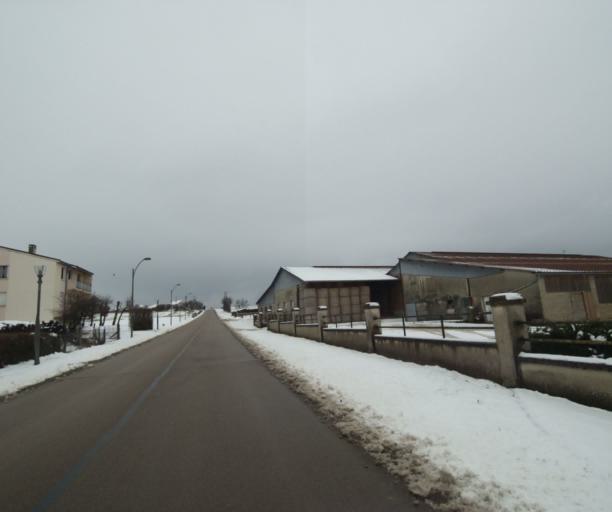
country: FR
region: Champagne-Ardenne
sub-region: Departement de la Haute-Marne
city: Laneuville-a-Remy
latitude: 48.4172
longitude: 4.8377
